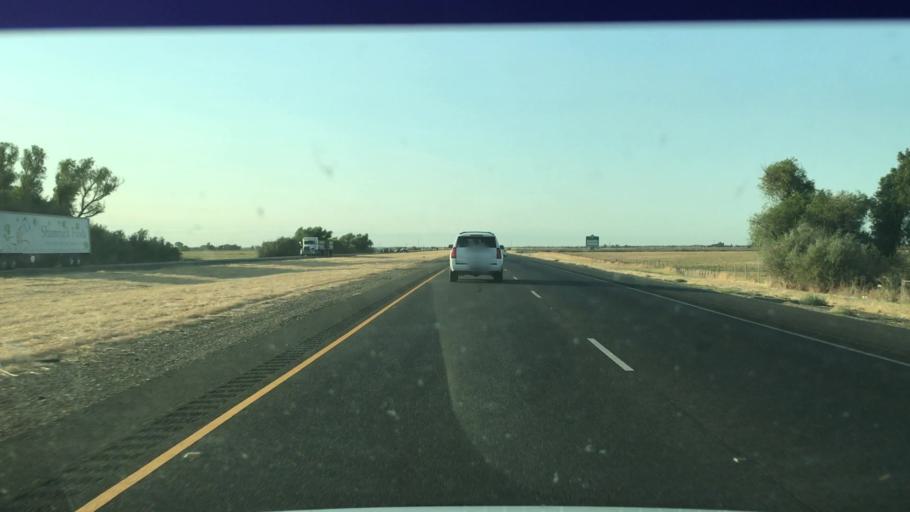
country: US
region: California
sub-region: Sacramento County
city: Laguna
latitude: 38.3454
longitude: -121.4704
